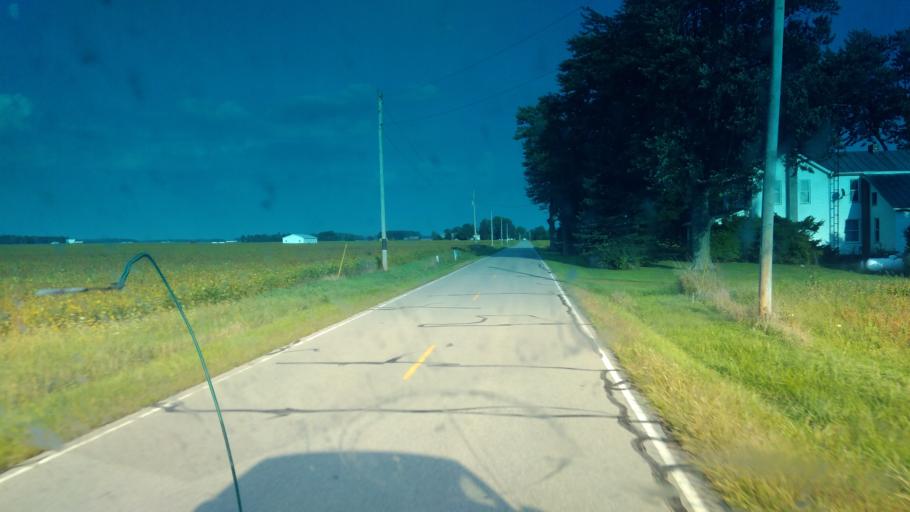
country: US
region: Ohio
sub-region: Crawford County
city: Bucyrus
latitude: 40.9649
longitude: -83.0321
